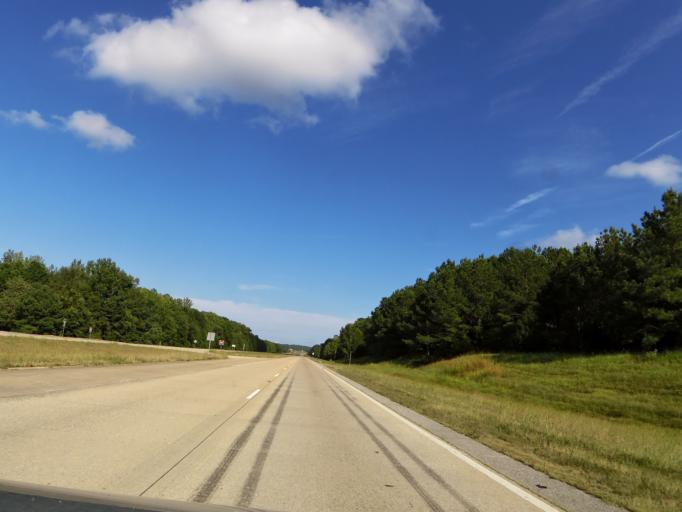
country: US
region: Mississippi
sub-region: Tishomingo County
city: Iuka
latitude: 34.8062
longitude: -88.2571
